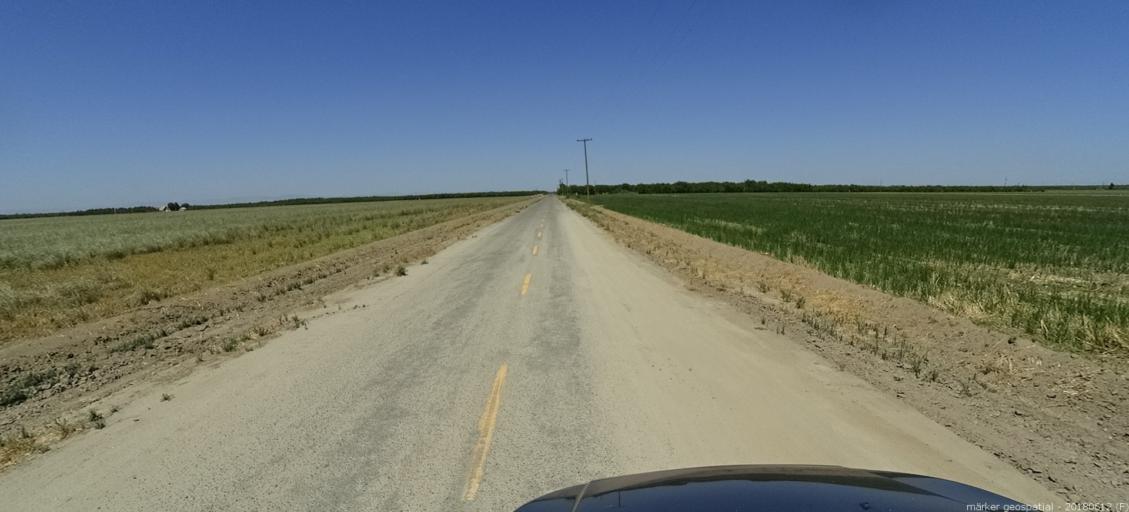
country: US
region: California
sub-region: Madera County
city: Chowchilla
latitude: 37.0470
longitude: -120.3741
